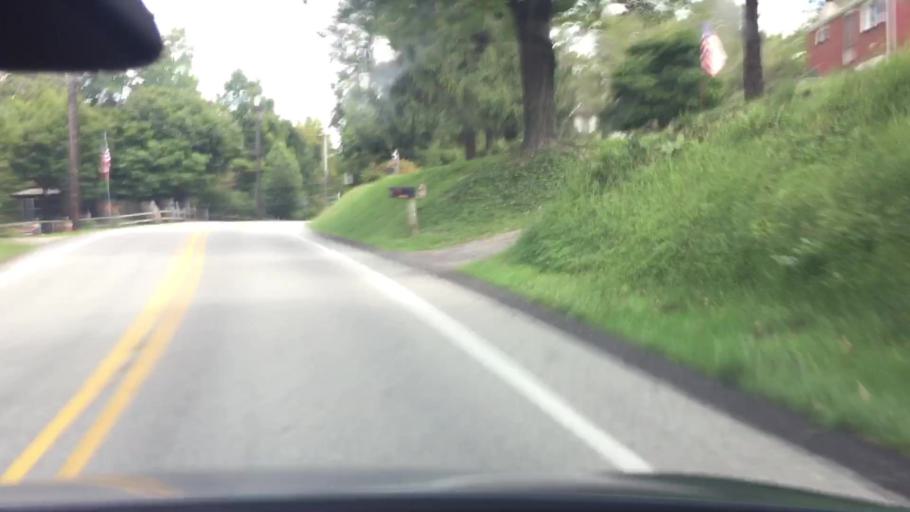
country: US
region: Pennsylvania
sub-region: Allegheny County
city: Penn Hills
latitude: 40.4956
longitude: -79.8063
